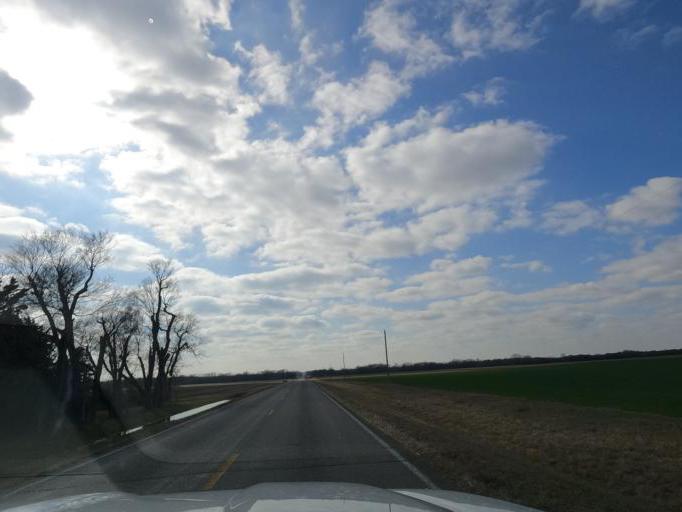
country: US
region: Kansas
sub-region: McPherson County
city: Inman
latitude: 38.2319
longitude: -97.8533
